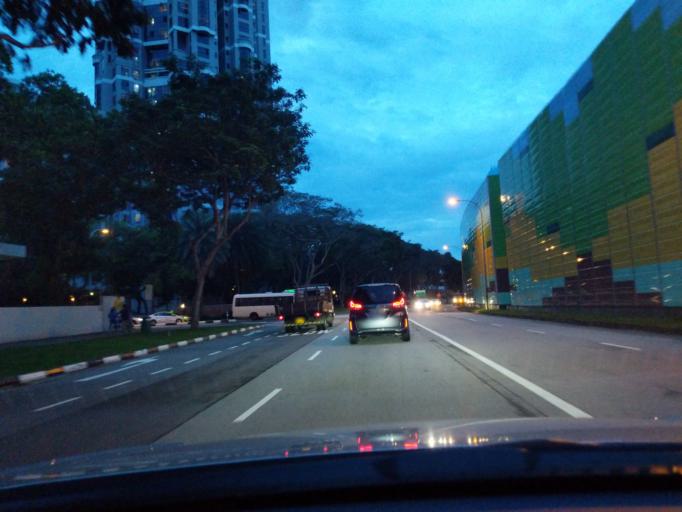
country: SG
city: Singapore
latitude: 1.3121
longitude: 103.9407
